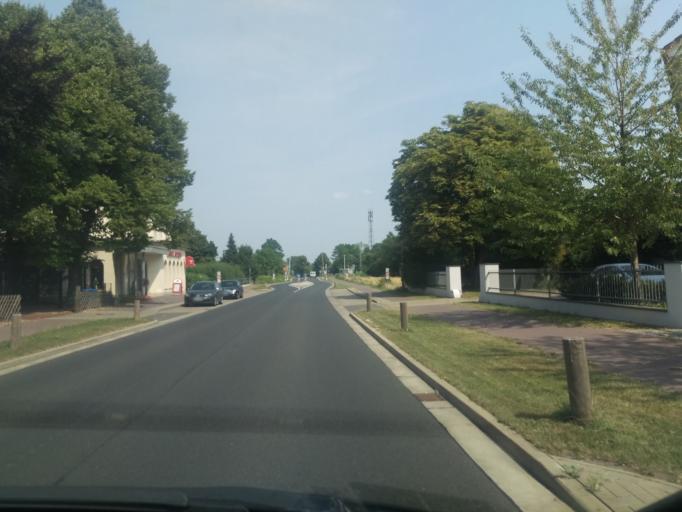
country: DE
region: Lower Saxony
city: Schellerten
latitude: 52.1892
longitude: 10.1060
